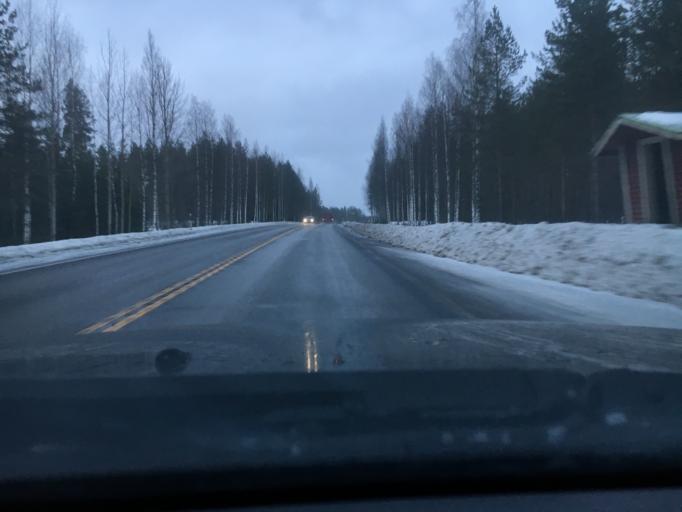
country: FI
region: Central Finland
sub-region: Jyvaeskylae
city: Hankasalmi
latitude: 62.3975
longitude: 26.6449
